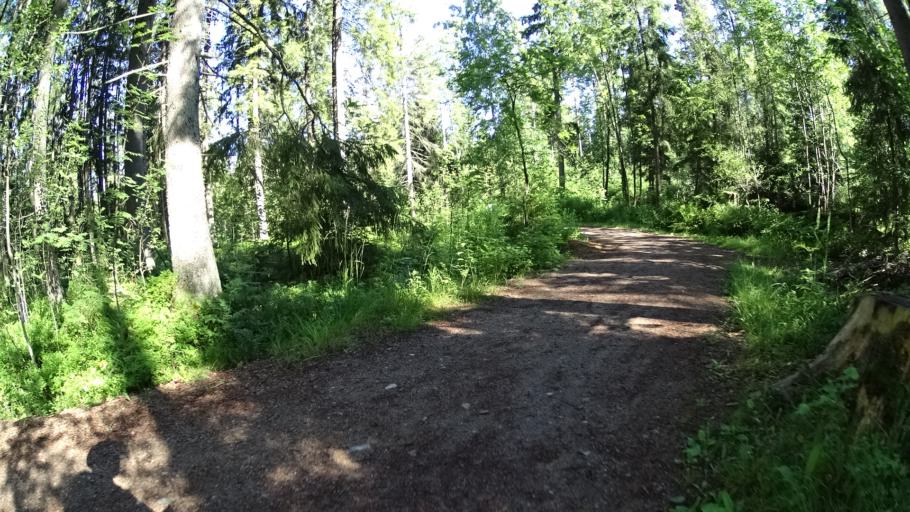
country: FI
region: Uusimaa
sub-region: Helsinki
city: Espoo
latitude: 60.2141
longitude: 24.6861
